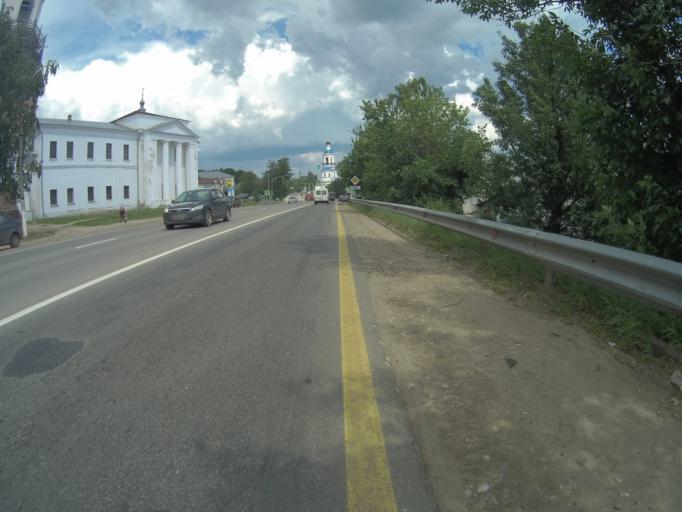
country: RU
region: Vladimir
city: Bogolyubovo
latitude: 56.1941
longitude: 40.5316
